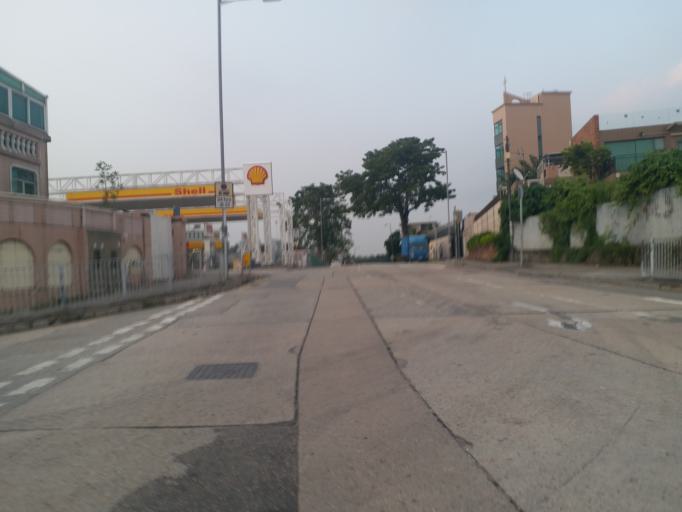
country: HK
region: Yuen Long
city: Yuen Long Kau Hui
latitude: 22.4393
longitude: 114.0111
